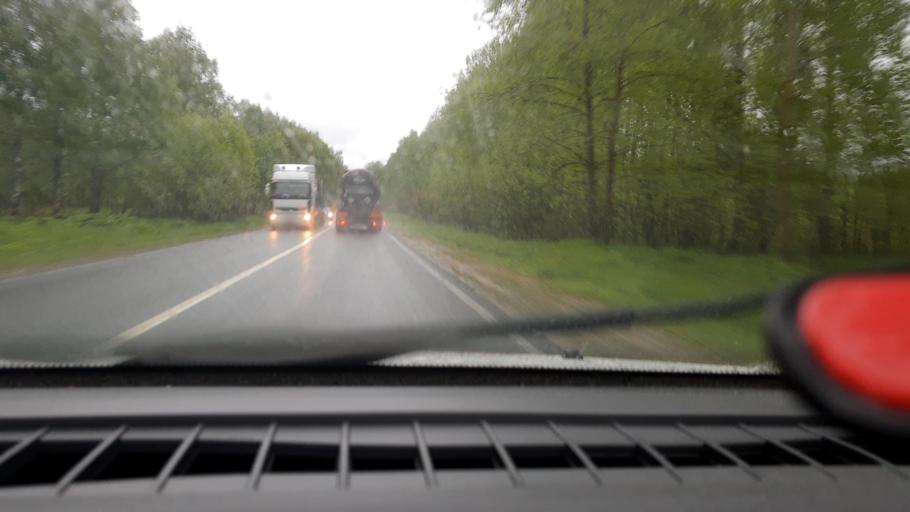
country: RU
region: Nizjnij Novgorod
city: Sukhobezvodnoye
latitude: 56.8634
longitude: 44.9060
